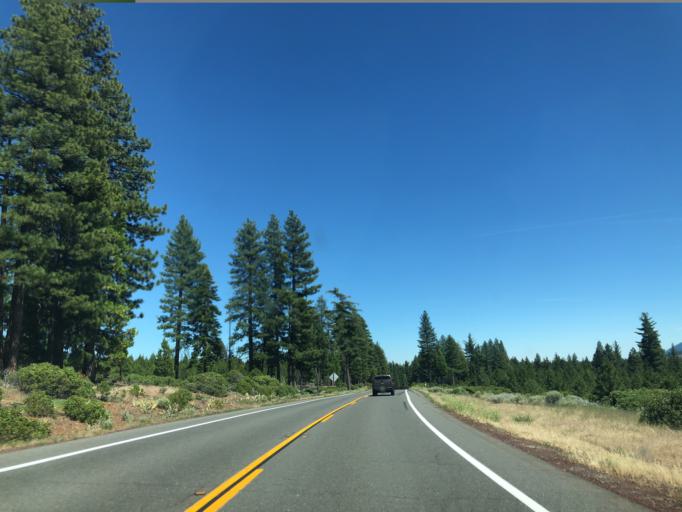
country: US
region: California
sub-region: Lassen County
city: Susanville
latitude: 40.4268
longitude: -120.7980
